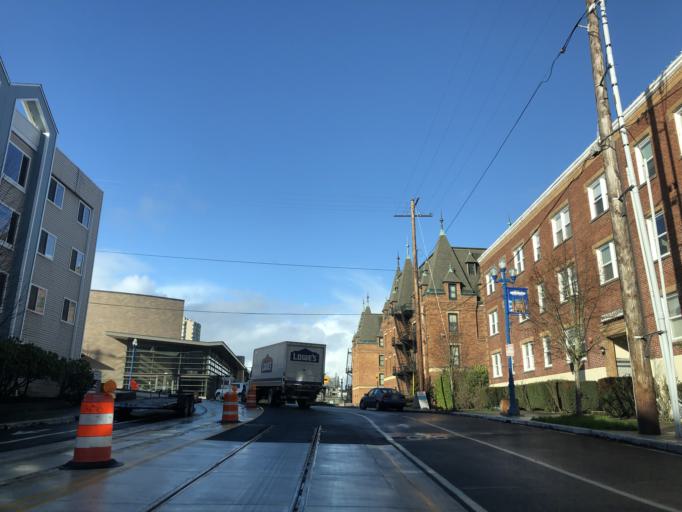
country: US
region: Washington
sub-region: Pierce County
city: Tacoma
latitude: 47.2653
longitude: -122.4472
